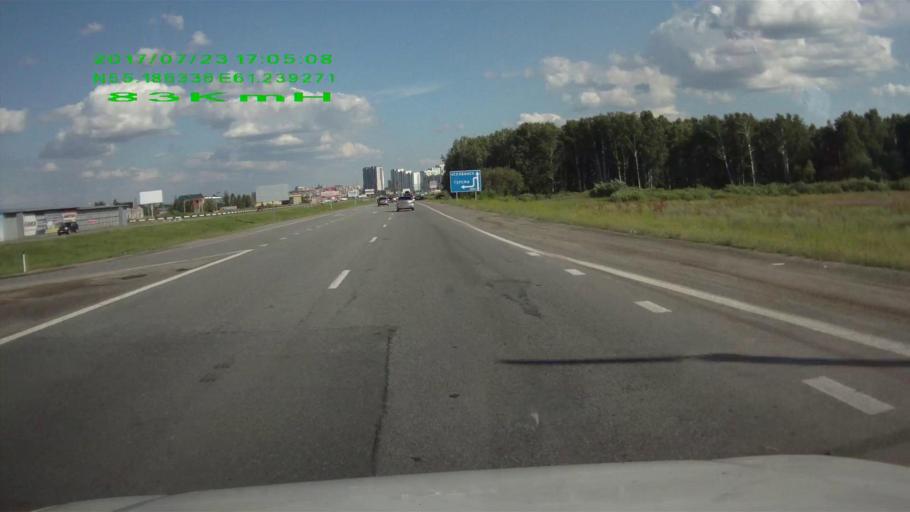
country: RU
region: Chelyabinsk
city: Roshchino
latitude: 55.1859
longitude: 61.2403
